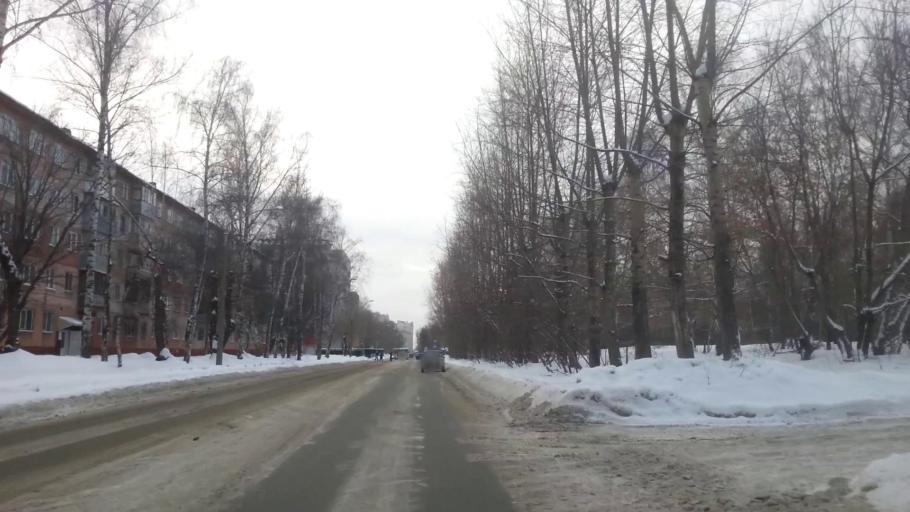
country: RU
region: Altai Krai
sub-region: Gorod Barnaulskiy
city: Barnaul
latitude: 53.3667
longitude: 83.6931
